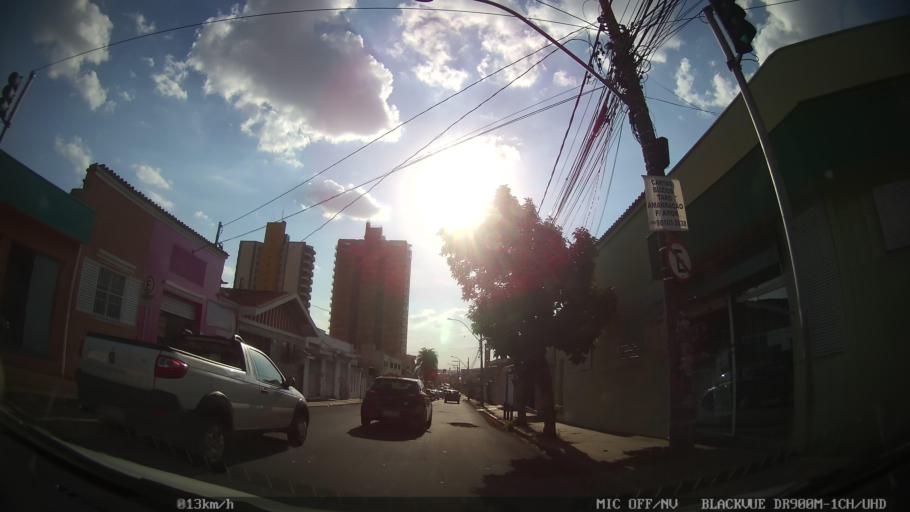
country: BR
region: Sao Paulo
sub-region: Ribeirao Preto
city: Ribeirao Preto
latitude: -21.1680
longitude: -47.8023
